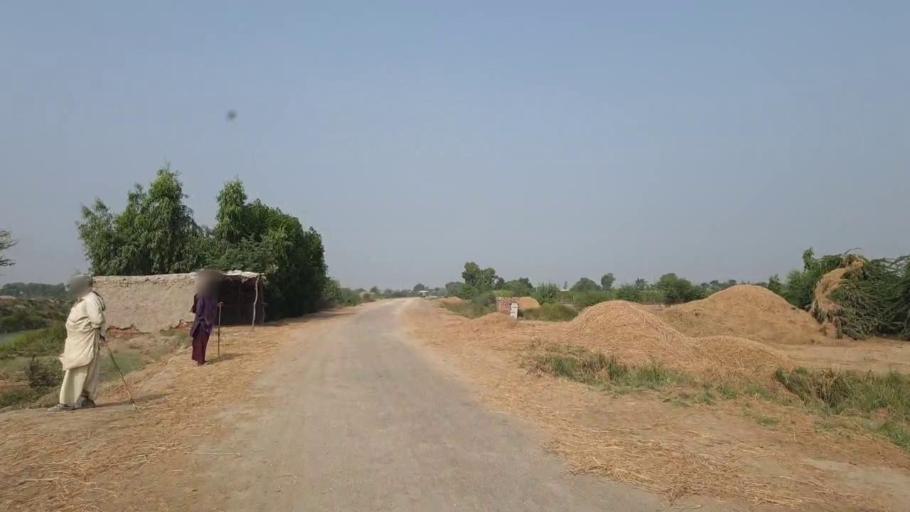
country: PK
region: Sindh
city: Kario
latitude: 24.9198
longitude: 68.6013
